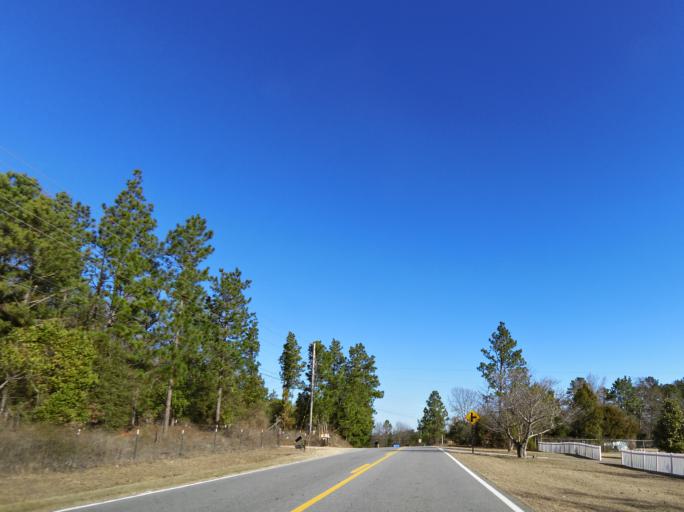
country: US
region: Georgia
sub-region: Bibb County
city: West Point
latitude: 32.7766
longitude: -83.7552
